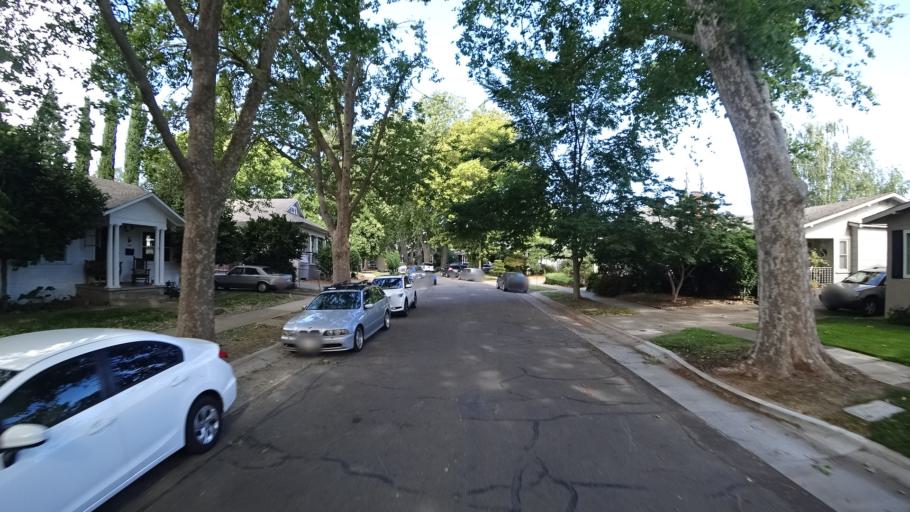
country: US
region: California
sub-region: Sacramento County
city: Sacramento
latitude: 38.5507
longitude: -121.5069
